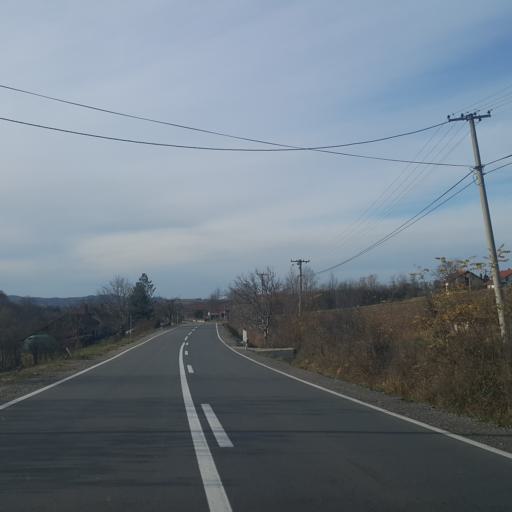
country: RS
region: Central Serbia
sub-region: Sumadijski Okrug
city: Arangelovac
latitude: 44.3379
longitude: 20.4254
